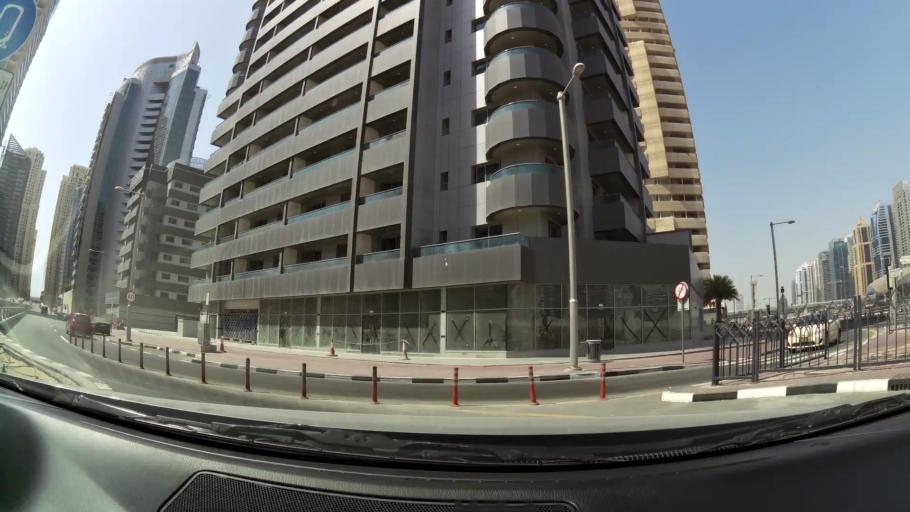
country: AE
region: Dubai
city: Dubai
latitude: 25.0695
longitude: 55.1352
